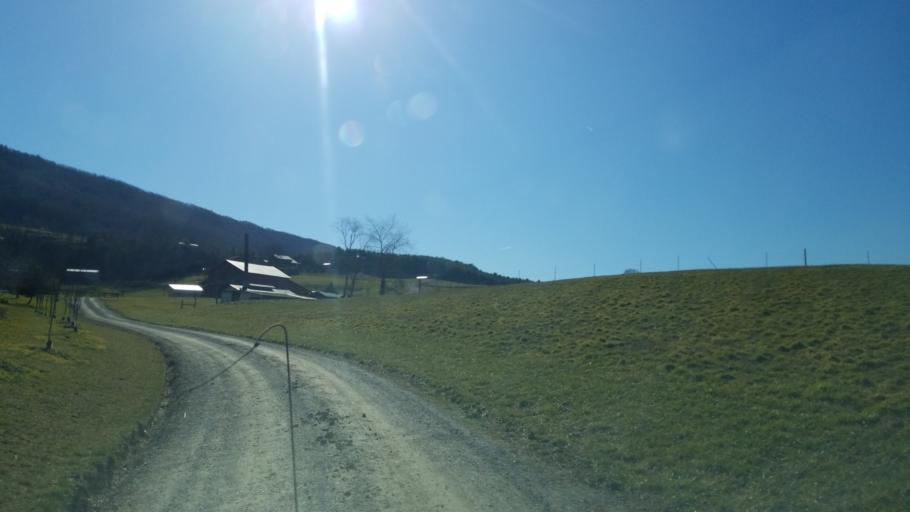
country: US
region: Virginia
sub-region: Pulaski County
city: Pulaski
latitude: 37.1599
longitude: -80.8598
